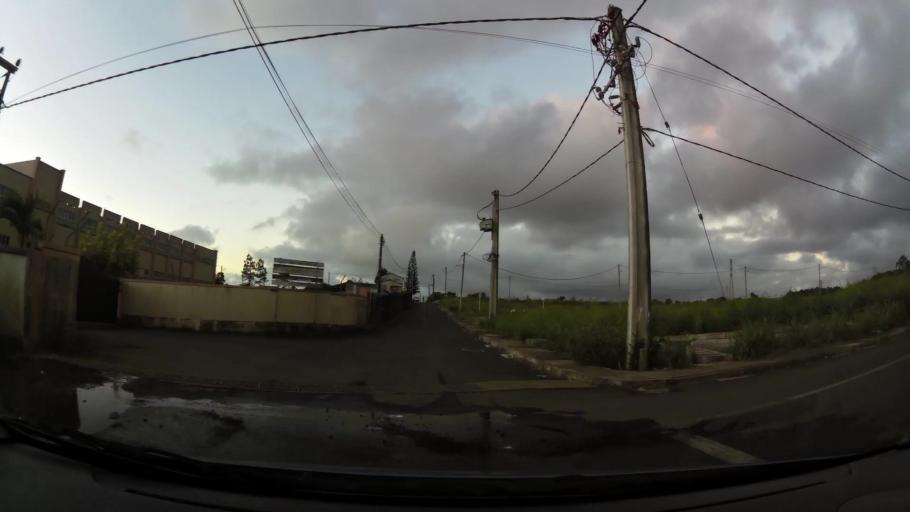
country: MU
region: Plaines Wilhems
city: Curepipe
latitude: -20.2975
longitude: 57.5314
